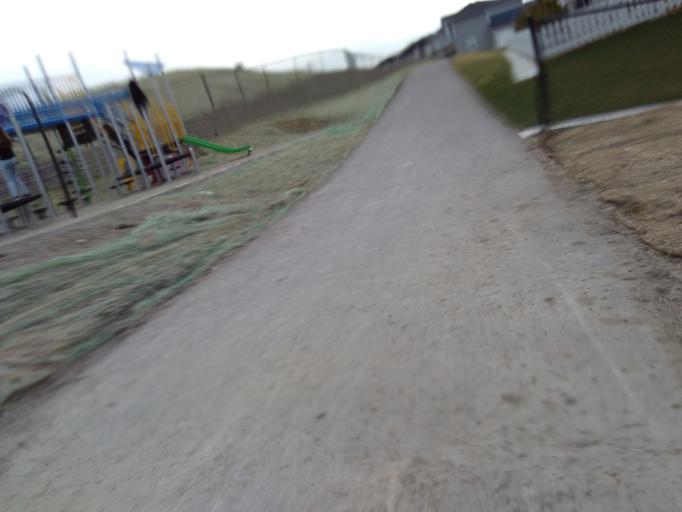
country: CA
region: Alberta
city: Cochrane
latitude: 51.1825
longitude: -114.5079
